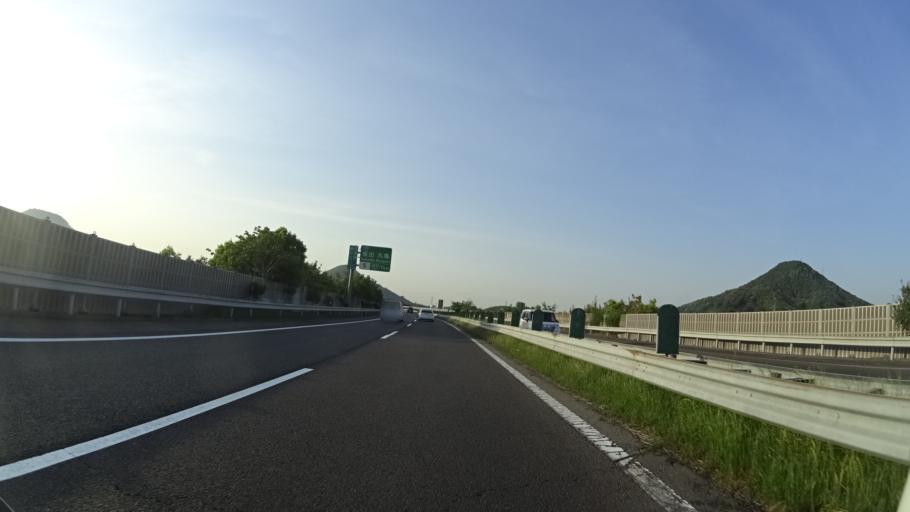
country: JP
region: Kagawa
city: Sakaidecho
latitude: 34.2867
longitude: 133.8516
